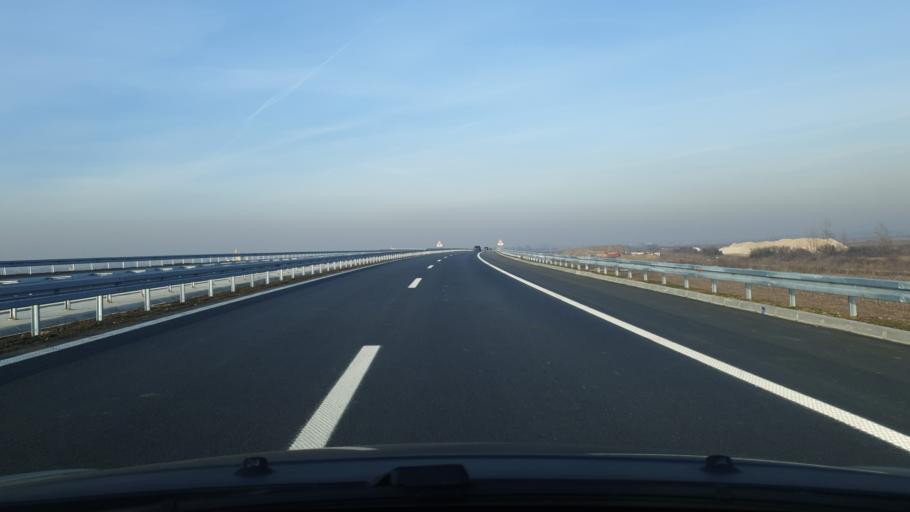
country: RS
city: Boljevci
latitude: 44.7147
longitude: 20.2587
